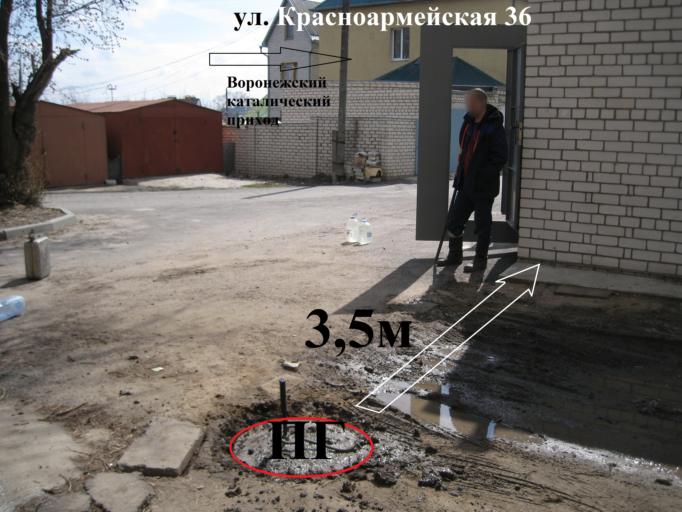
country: RU
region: Voronezj
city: Voronezh
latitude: 51.6503
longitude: 39.1953
